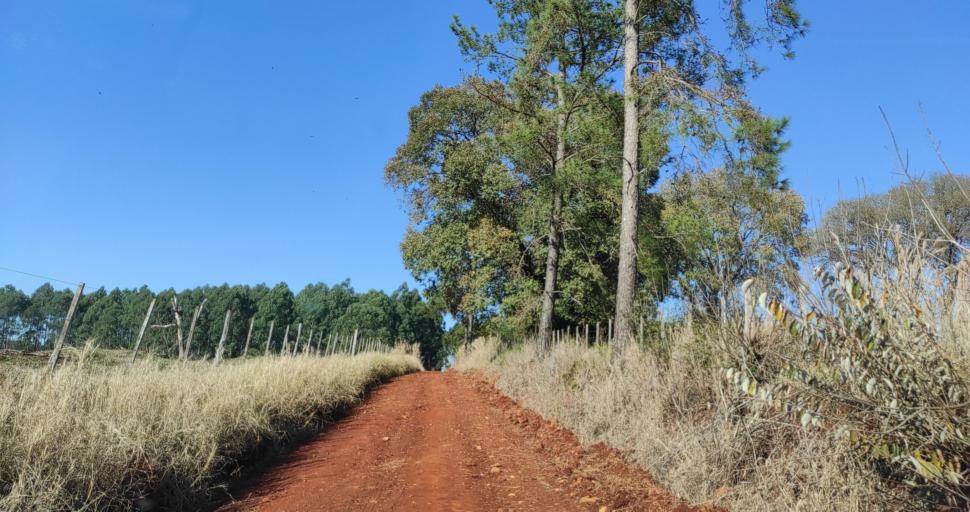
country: AR
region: Misiones
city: Capiovi
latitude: -26.8763
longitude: -55.0366
